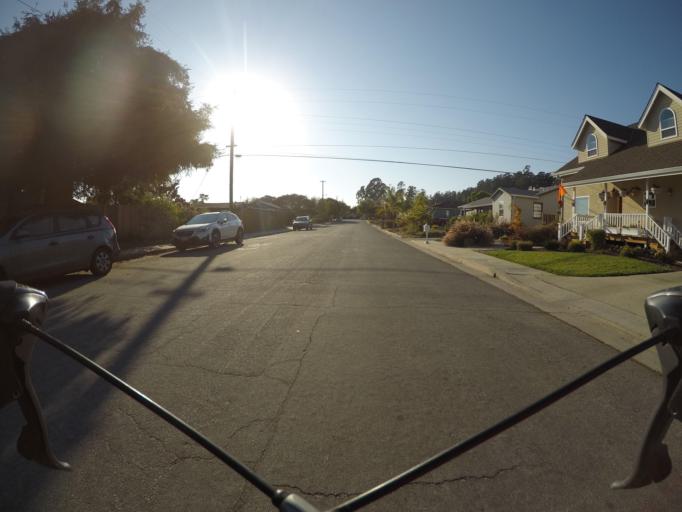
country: US
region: California
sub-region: Santa Cruz County
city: Live Oak
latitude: 36.9901
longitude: -122.0002
